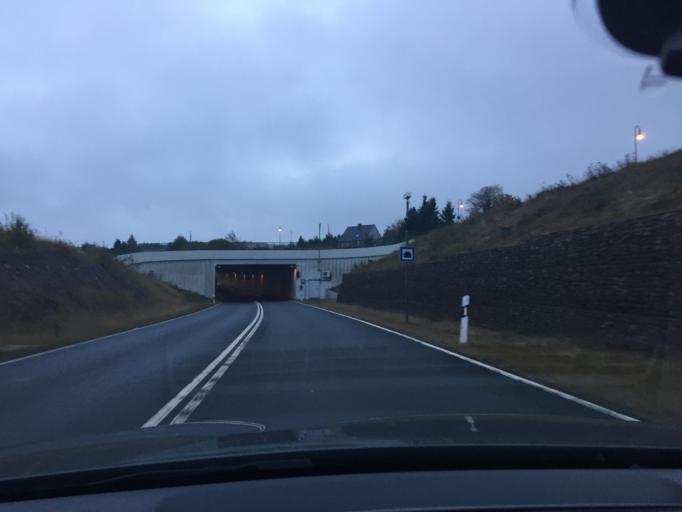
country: DE
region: Saxony
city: Altenberg
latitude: 50.7381
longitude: 13.7548
